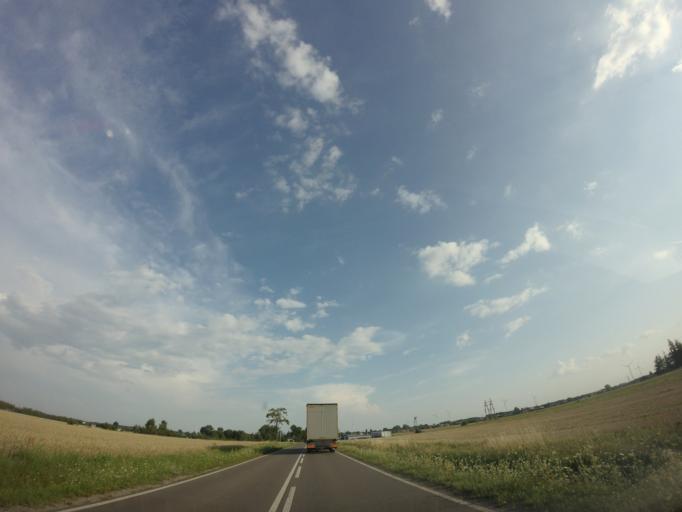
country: PL
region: Lublin Voivodeship
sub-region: Powiat lubartowski
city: Michow
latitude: 51.5341
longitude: 22.3112
